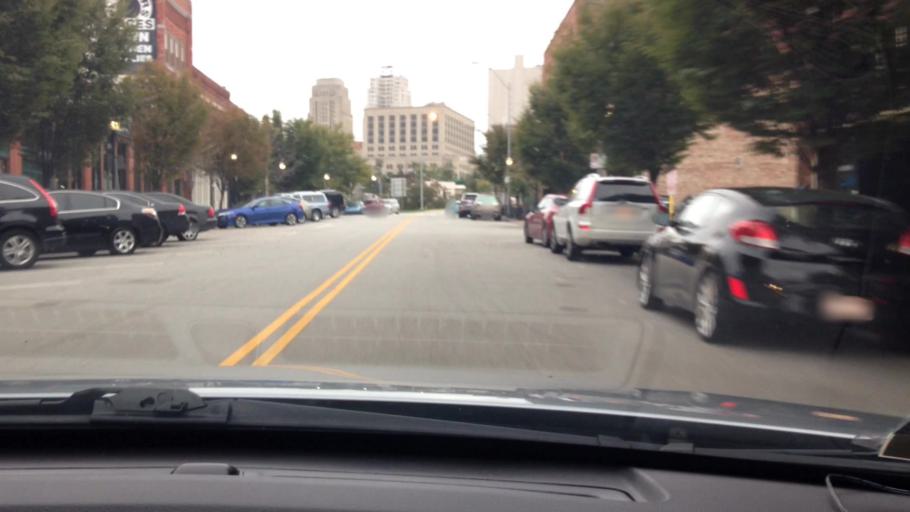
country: US
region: Missouri
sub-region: Jackson County
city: Kansas City
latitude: 39.1083
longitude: -94.5816
